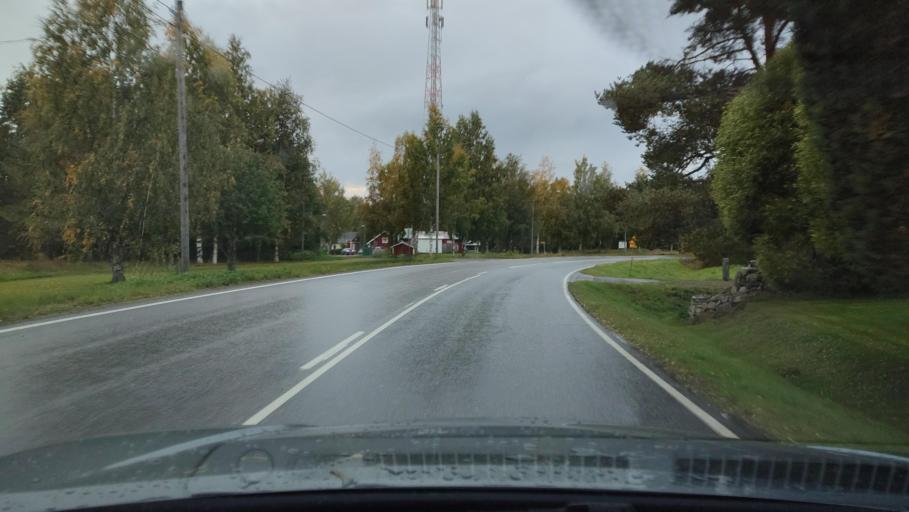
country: FI
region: Southern Ostrobothnia
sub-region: Suupohja
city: Karijoki
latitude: 62.2417
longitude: 21.5727
